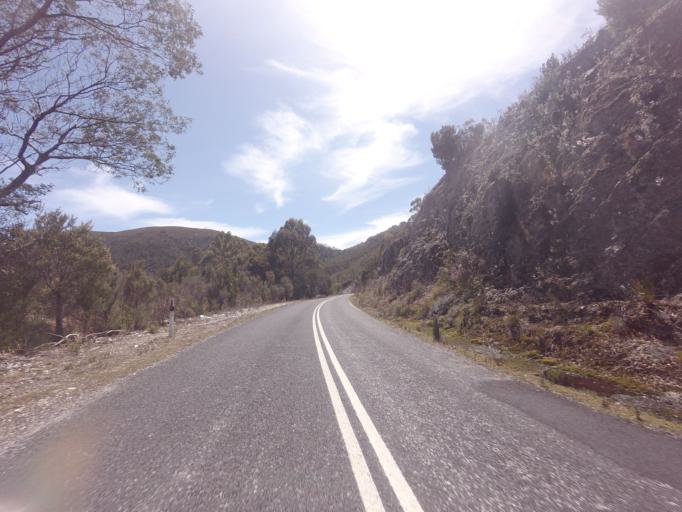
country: AU
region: Tasmania
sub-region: West Coast
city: Queenstown
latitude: -42.7965
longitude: 146.0870
